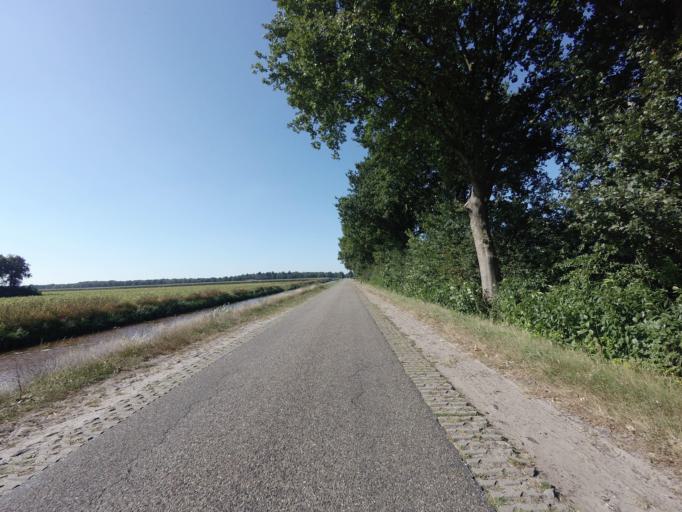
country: NL
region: Overijssel
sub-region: Gemeente Hardenberg
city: Hardenberg
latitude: 52.5271
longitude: 6.6497
